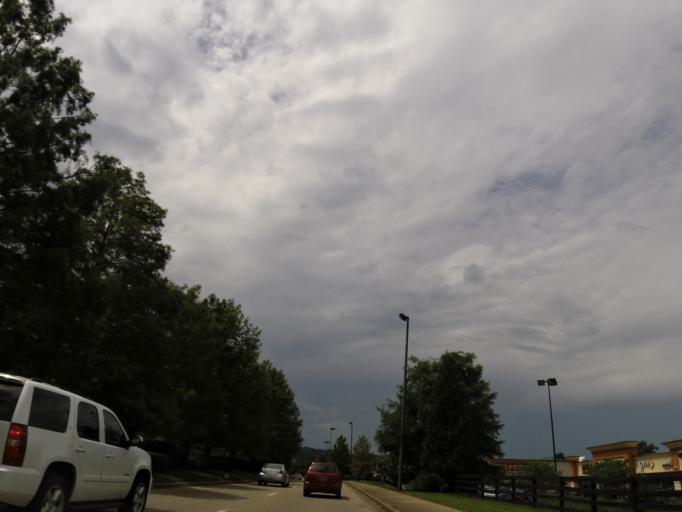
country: US
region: Tennessee
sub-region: Knox County
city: Farragut
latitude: 35.9017
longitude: -84.1460
